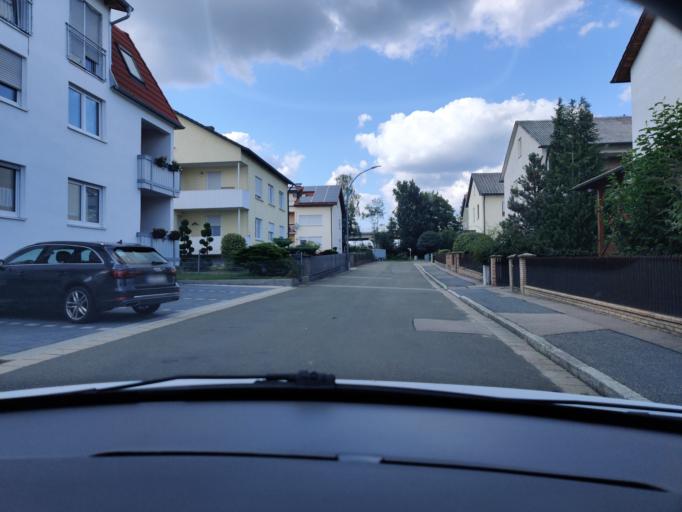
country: DE
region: Bavaria
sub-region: Upper Palatinate
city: Schwarzenfeld
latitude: 49.3874
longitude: 12.1248
